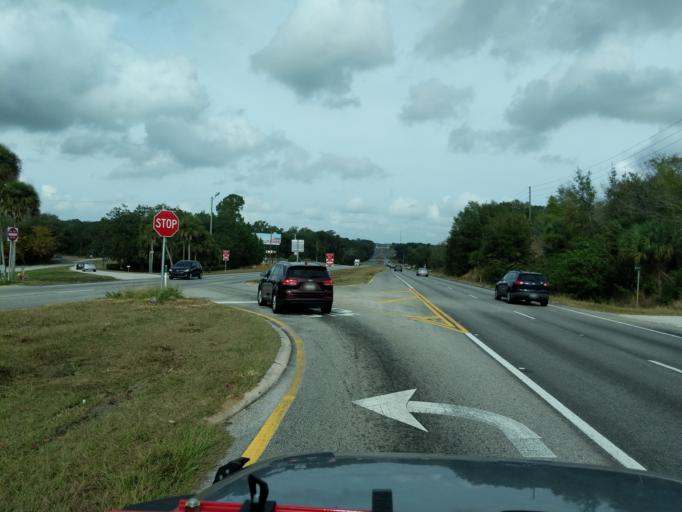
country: US
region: Florida
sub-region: Orange County
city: Tangerine
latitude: 28.7766
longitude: -81.6243
